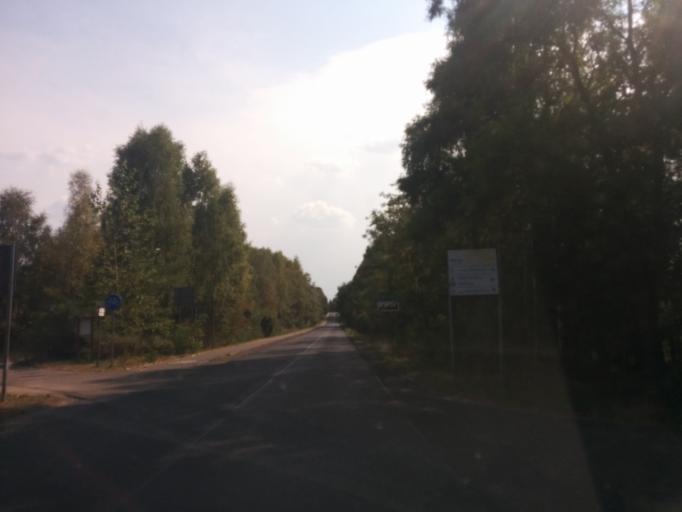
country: PL
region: Silesian Voivodeship
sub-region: Powiat czestochowski
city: Olsztyn
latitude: 50.7399
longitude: 19.2658
